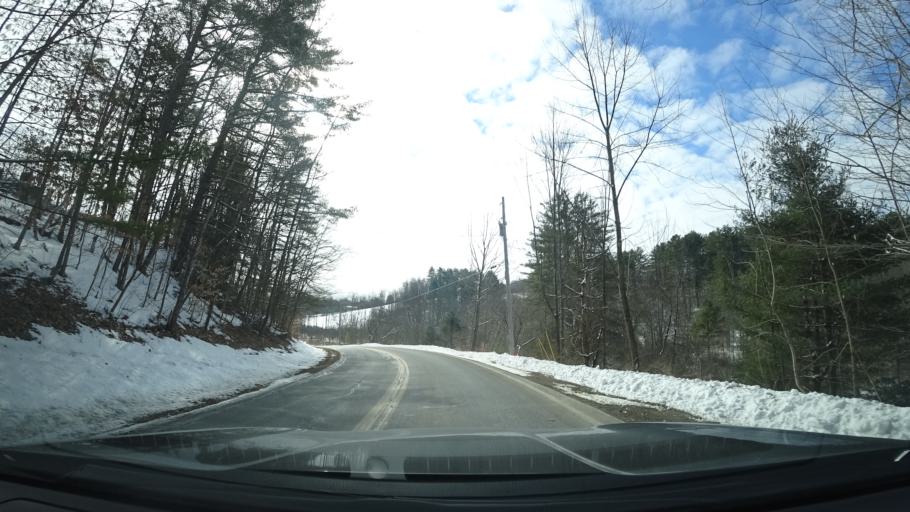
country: US
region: New York
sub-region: Washington County
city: Fort Edward
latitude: 43.2487
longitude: -73.4155
